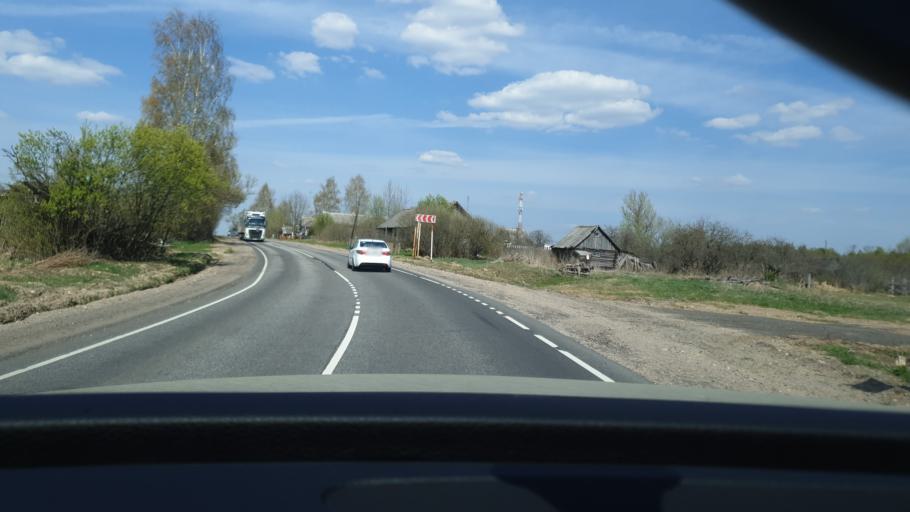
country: RU
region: Moskovskaya
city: Mikulino
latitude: 56.5208
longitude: 35.7199
